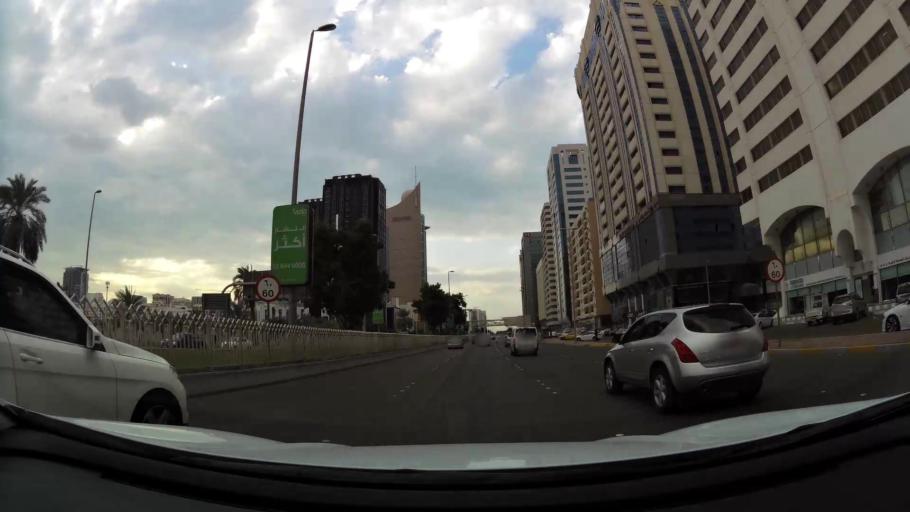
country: AE
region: Abu Dhabi
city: Abu Dhabi
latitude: 24.4781
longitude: 54.3635
